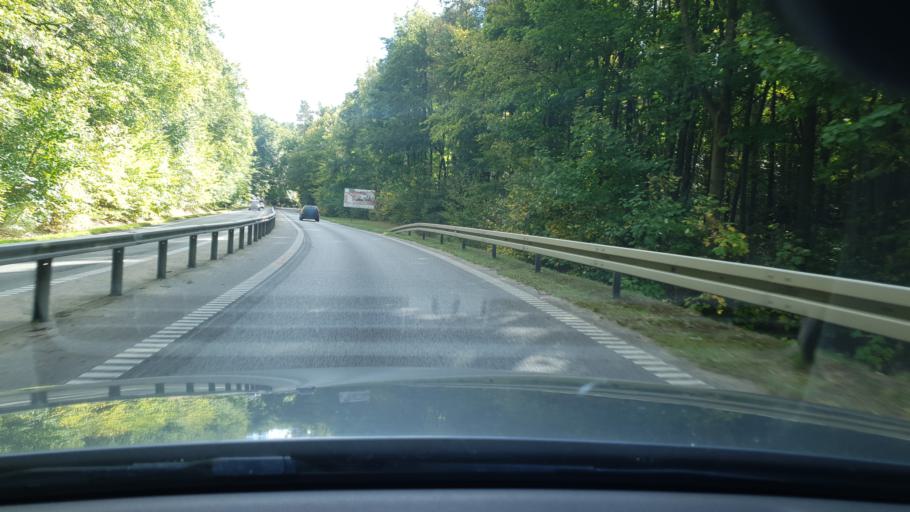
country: PL
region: Pomeranian Voivodeship
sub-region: Powiat wejherowski
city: Rekowo Dolne
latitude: 54.6319
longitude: 18.3440
